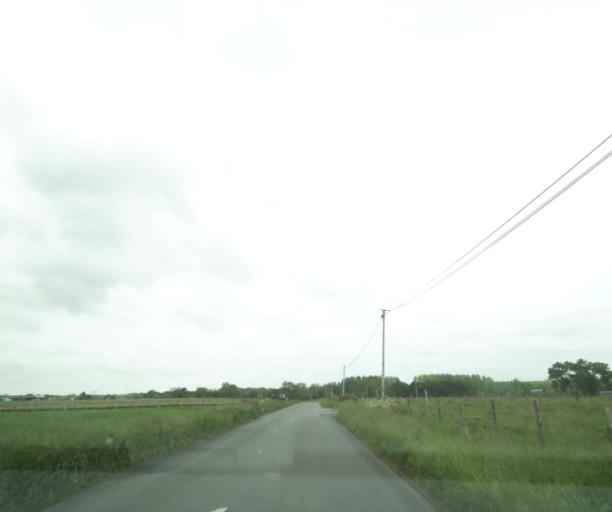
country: FR
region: Poitou-Charentes
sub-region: Departement de la Charente-Maritime
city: Chaniers
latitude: 45.7056
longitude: -0.5648
